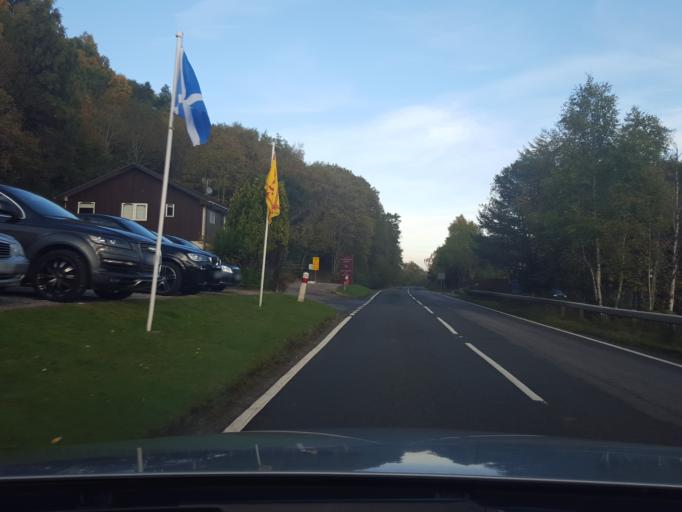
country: GB
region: Scotland
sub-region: Highland
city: Beauly
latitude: 57.3646
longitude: -4.3924
